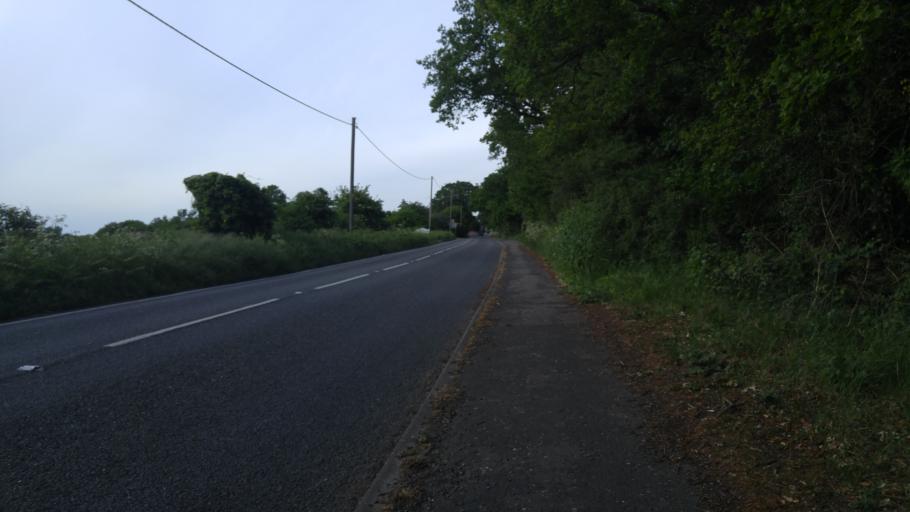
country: GB
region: England
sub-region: Essex
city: Layer de la Haye
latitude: 51.8615
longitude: 0.8688
